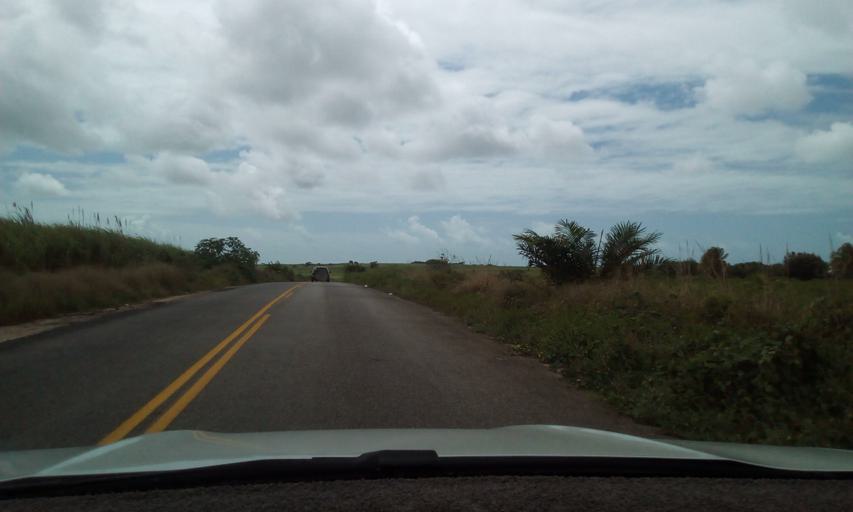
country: BR
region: Paraiba
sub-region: Rio Tinto
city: Rio Tinto
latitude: -6.7678
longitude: -35.0061
